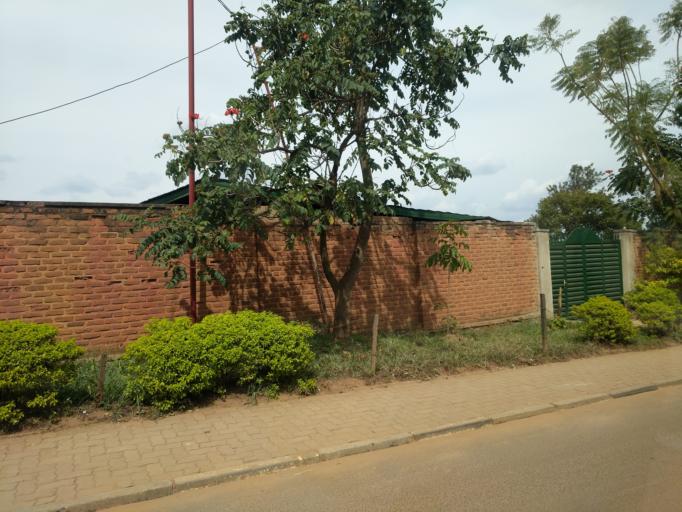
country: RW
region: Kigali
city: Kigali
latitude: -1.9814
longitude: 30.1169
